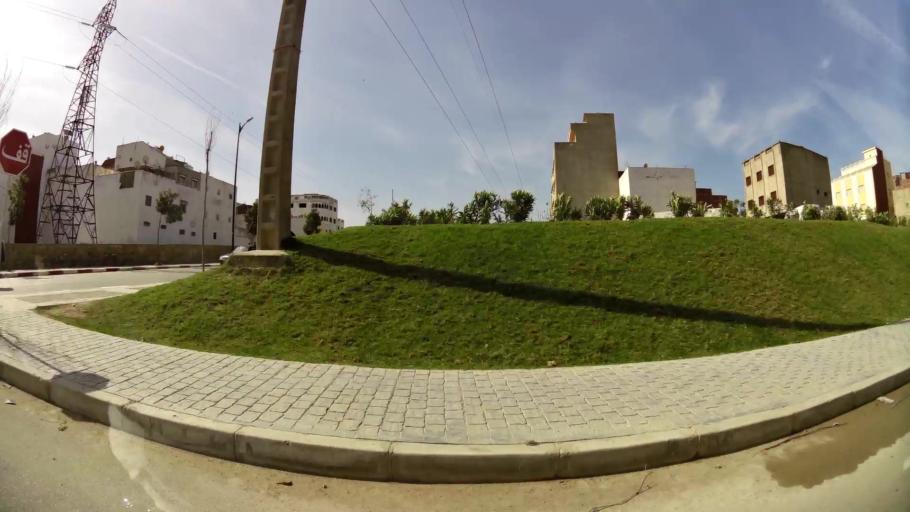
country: MA
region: Tanger-Tetouan
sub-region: Tanger-Assilah
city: Tangier
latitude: 35.7272
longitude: -5.8086
